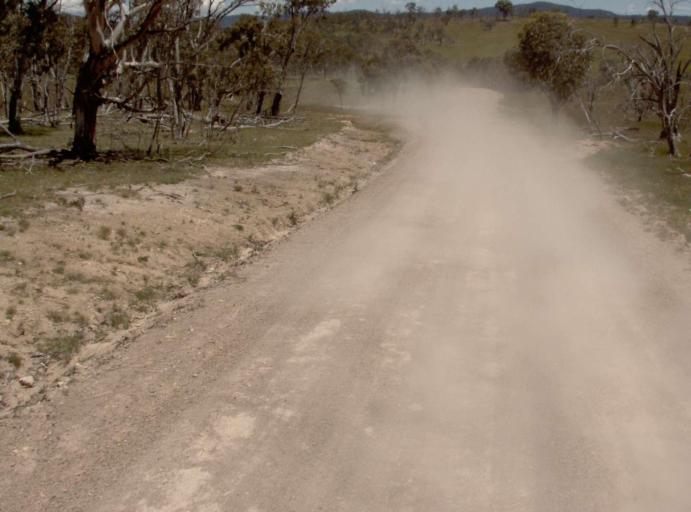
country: AU
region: New South Wales
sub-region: Snowy River
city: Jindabyne
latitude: -37.0587
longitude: 148.3020
